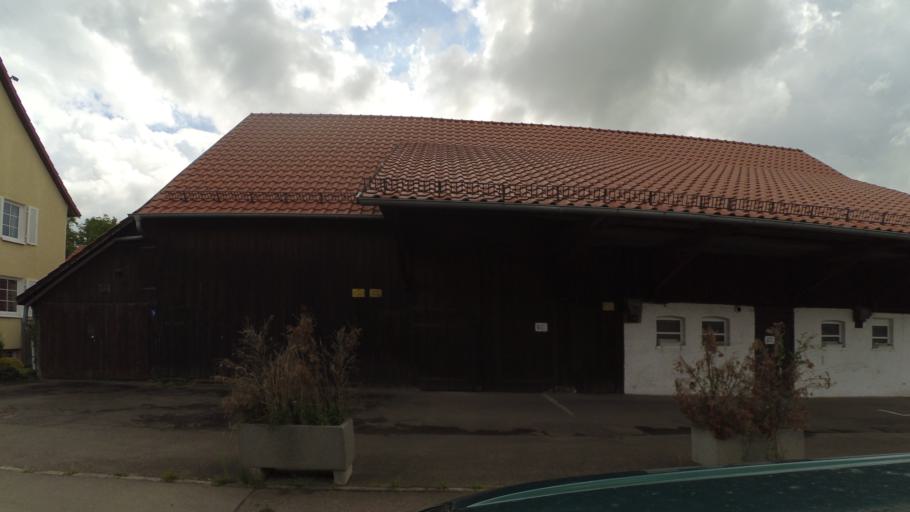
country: DE
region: Baden-Wuerttemberg
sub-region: Regierungsbezirk Stuttgart
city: Ottenbach
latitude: 48.7337
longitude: 9.7472
